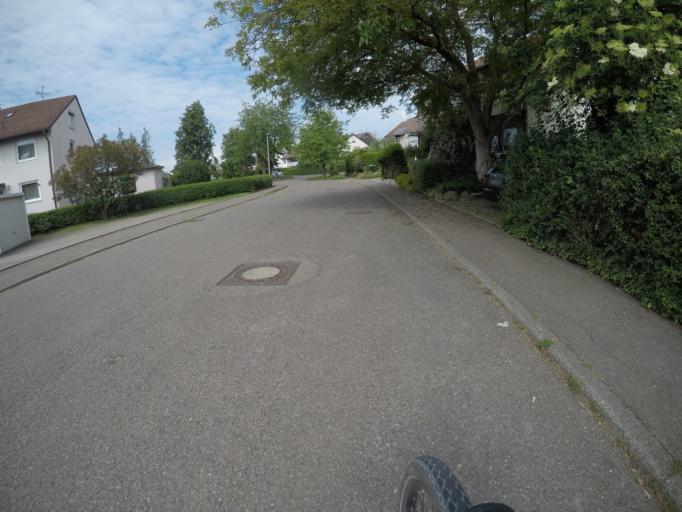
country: DE
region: Baden-Wuerttemberg
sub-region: Regierungsbezirk Stuttgart
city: Notzingen
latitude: 48.6709
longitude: 9.4541
